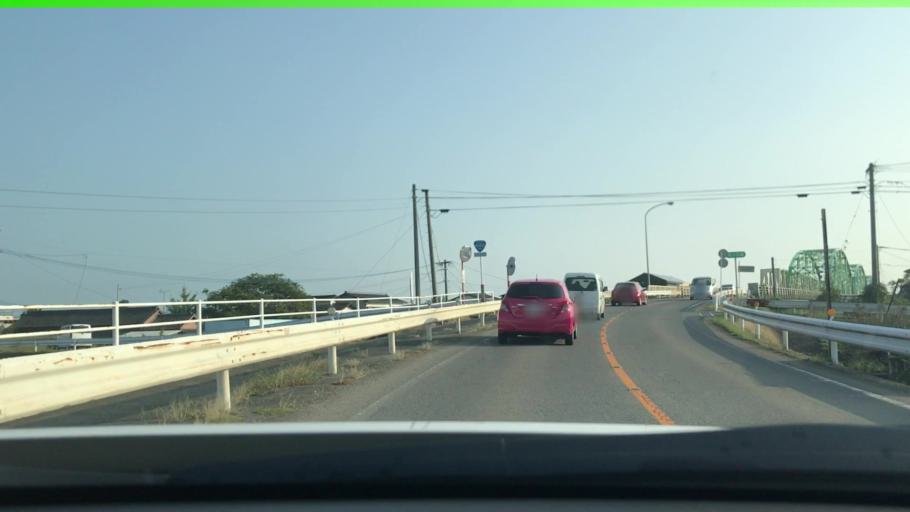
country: JP
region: Saga Prefecture
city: Saga-shi
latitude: 33.1990
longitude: 130.1939
